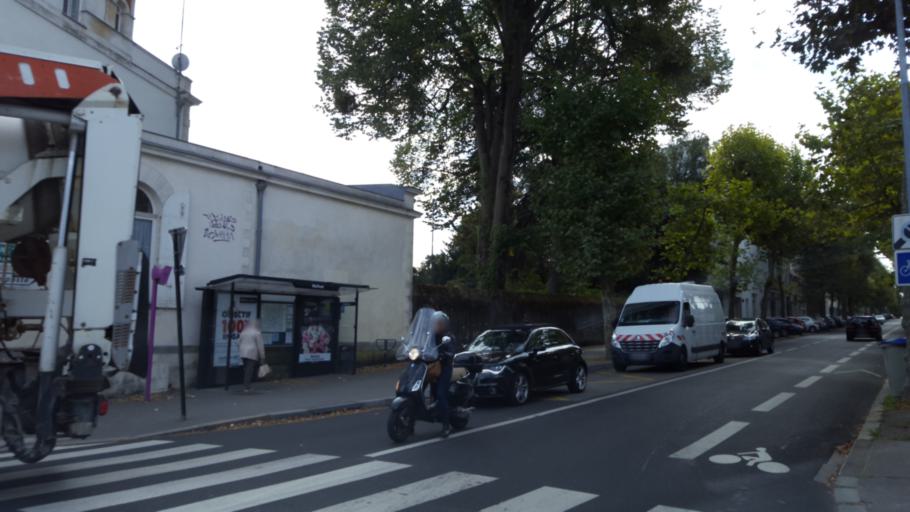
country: FR
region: Pays de la Loire
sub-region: Departement de la Loire-Atlantique
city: Nantes
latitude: 47.2110
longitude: -1.5766
